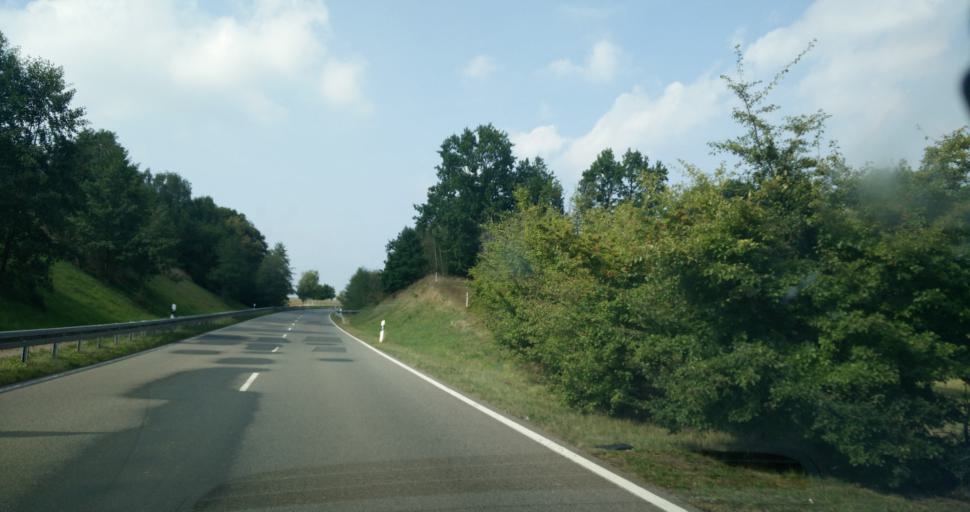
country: DE
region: Saxony
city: Rochlitz
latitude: 51.0621
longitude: 12.7850
